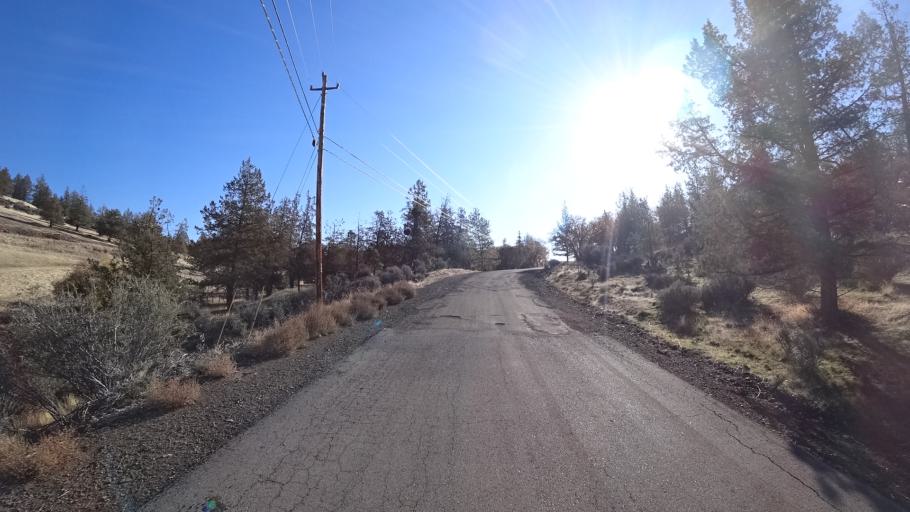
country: US
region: California
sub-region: Siskiyou County
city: Montague
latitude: 41.9149
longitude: -122.4348
